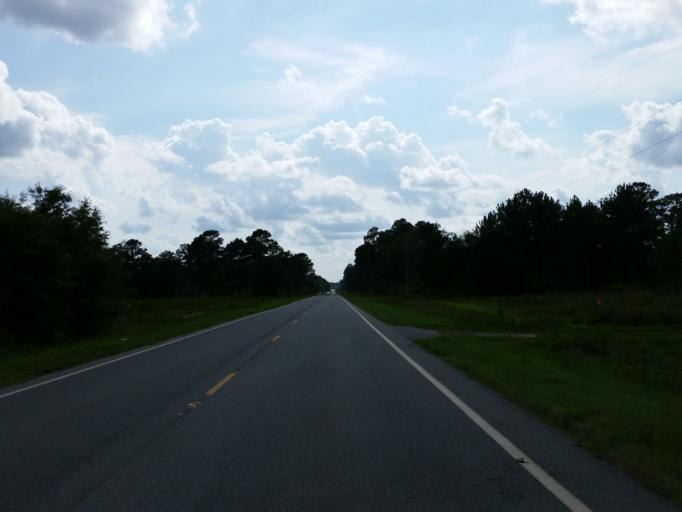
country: US
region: Georgia
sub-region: Lee County
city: Leesburg
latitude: 31.7273
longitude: -83.9778
